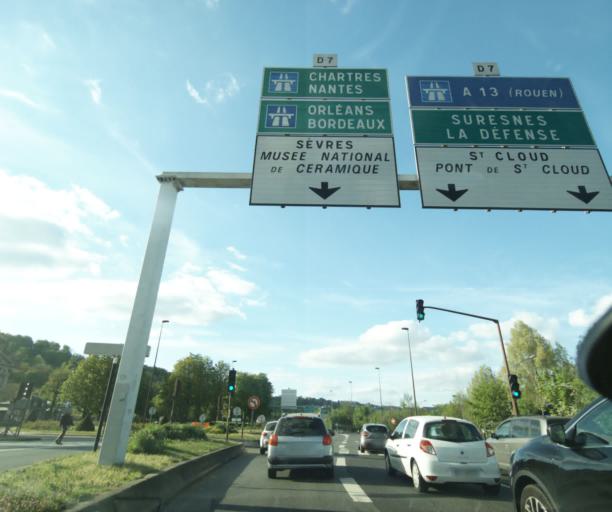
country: FR
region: Ile-de-France
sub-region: Departement des Hauts-de-Seine
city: Sevres
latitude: 48.8286
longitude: 2.2247
